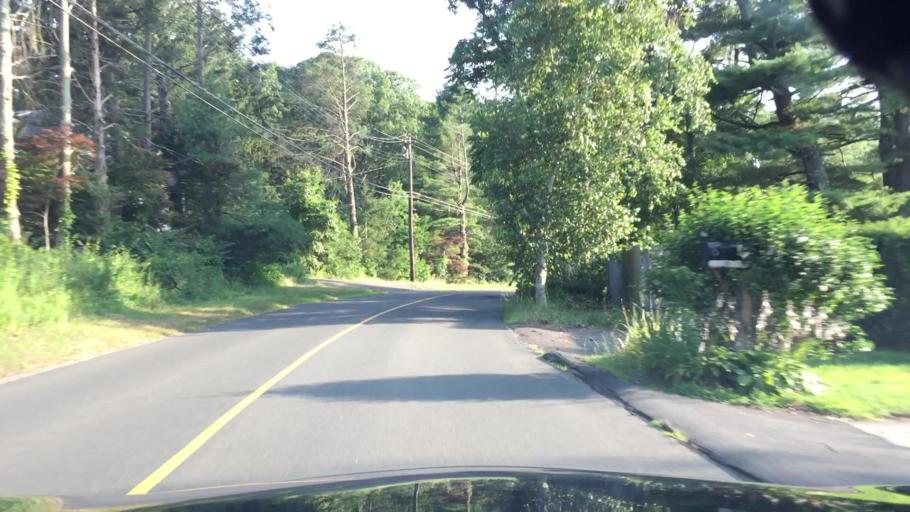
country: US
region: Connecticut
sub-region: New Haven County
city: Woodmont
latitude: 41.2499
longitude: -73.0086
